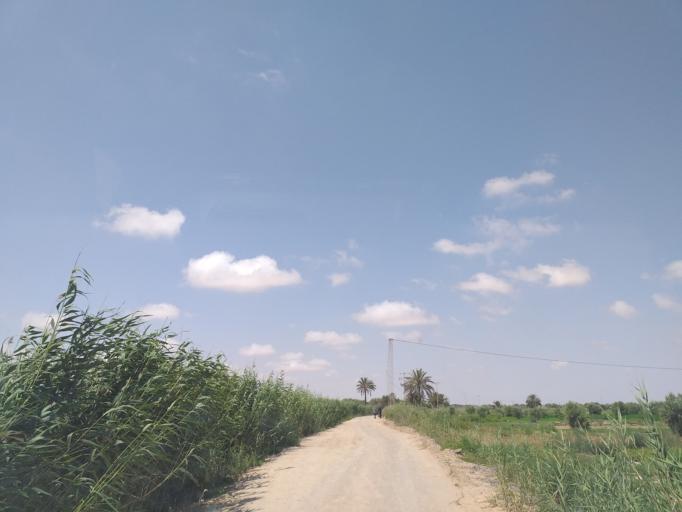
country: TN
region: Qabis
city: Gabes
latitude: 33.9533
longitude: 10.0466
